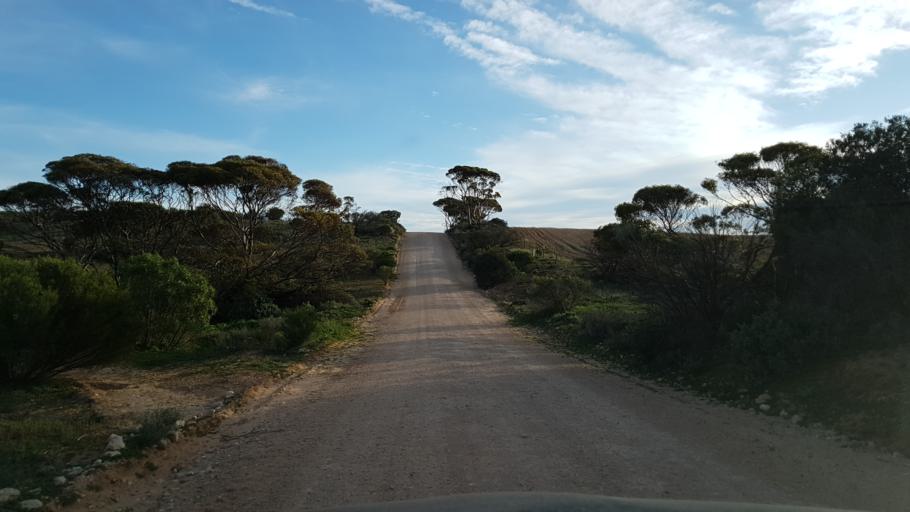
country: AU
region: South Australia
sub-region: Mid Murray
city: Mannum
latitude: -34.7526
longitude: 139.5741
